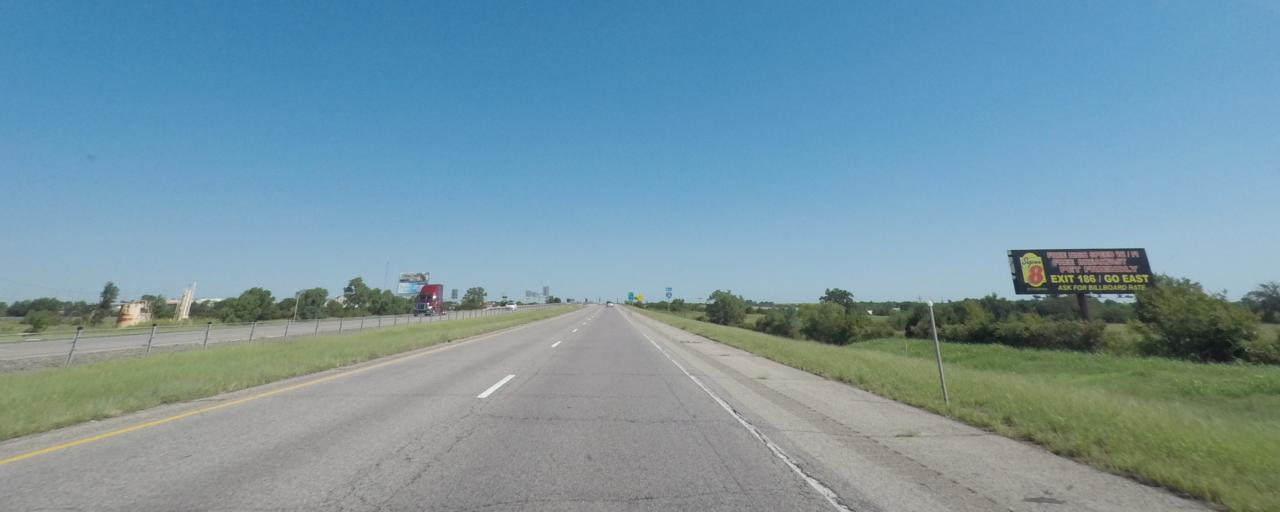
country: US
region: Oklahoma
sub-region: Noble County
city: Perry
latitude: 36.2810
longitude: -97.3276
